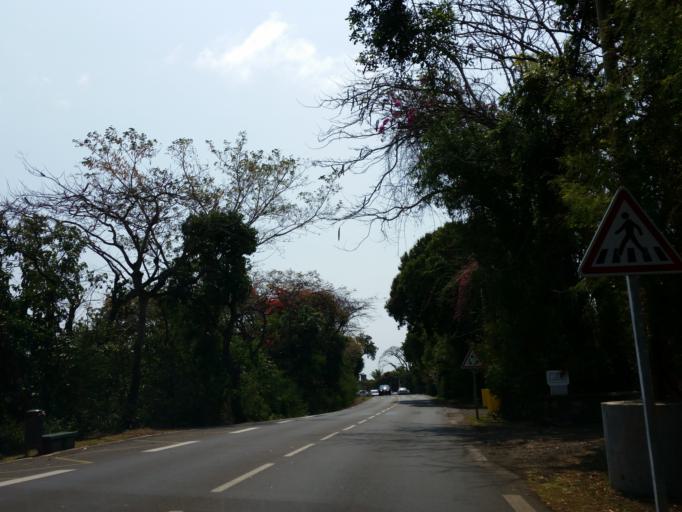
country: RE
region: Reunion
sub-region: Reunion
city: Sainte-Marie
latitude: -20.9041
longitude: 55.5070
